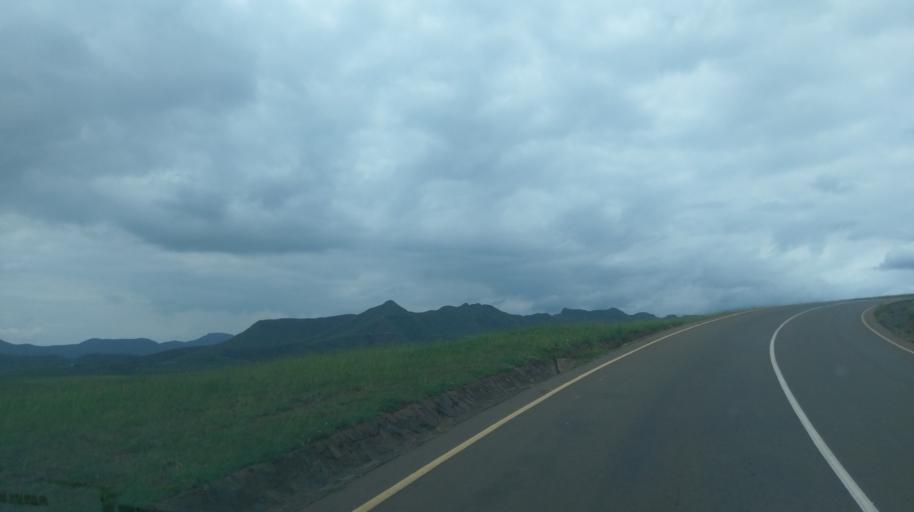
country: LS
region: Leribe
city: Leribe
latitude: -29.0330
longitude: 28.2540
